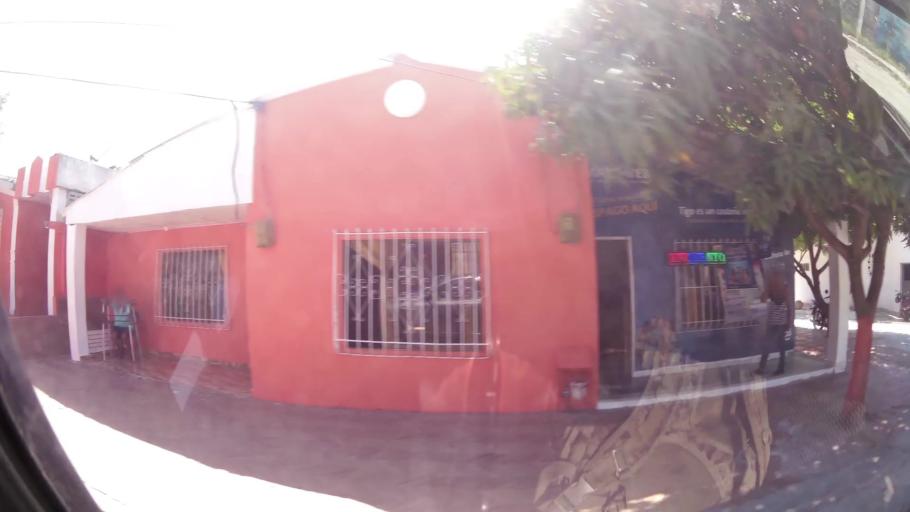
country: CO
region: Atlantico
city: Barranquilla
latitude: 10.9796
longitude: -74.8225
